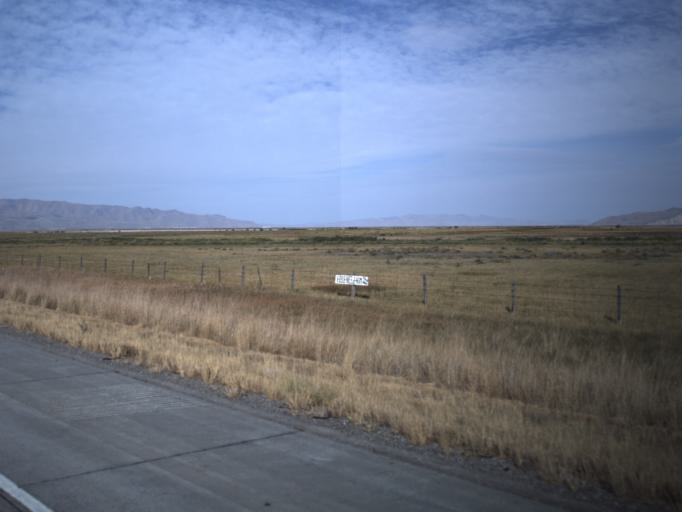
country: US
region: Utah
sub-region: Tooele County
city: Stansbury park
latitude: 40.6651
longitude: -112.3152
